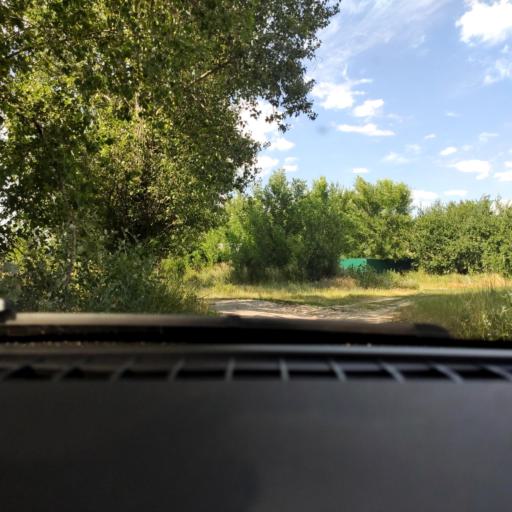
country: RU
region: Voronezj
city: Voronezh
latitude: 51.7030
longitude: 39.2650
